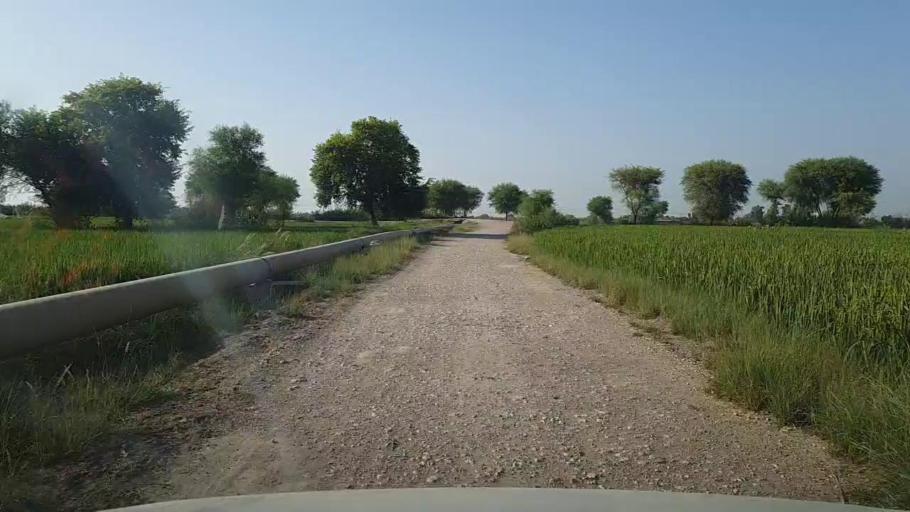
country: PK
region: Sindh
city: Kandhkot
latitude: 28.2880
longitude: 69.3324
